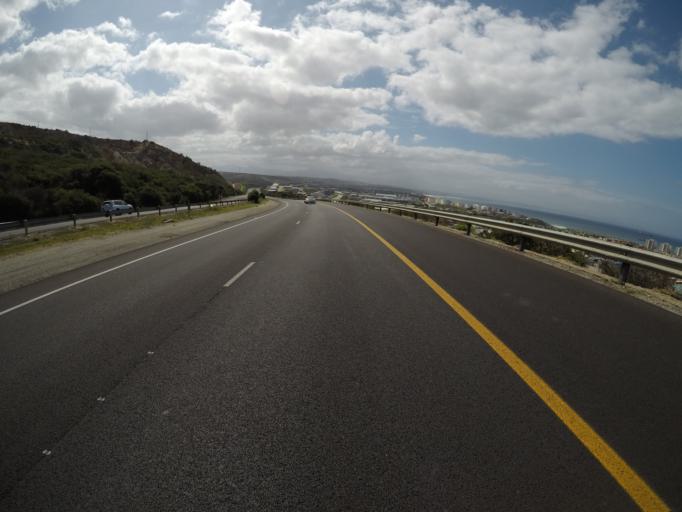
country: ZA
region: Western Cape
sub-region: Eden District Municipality
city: Mossel Bay
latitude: -34.1580
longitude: 22.0997
